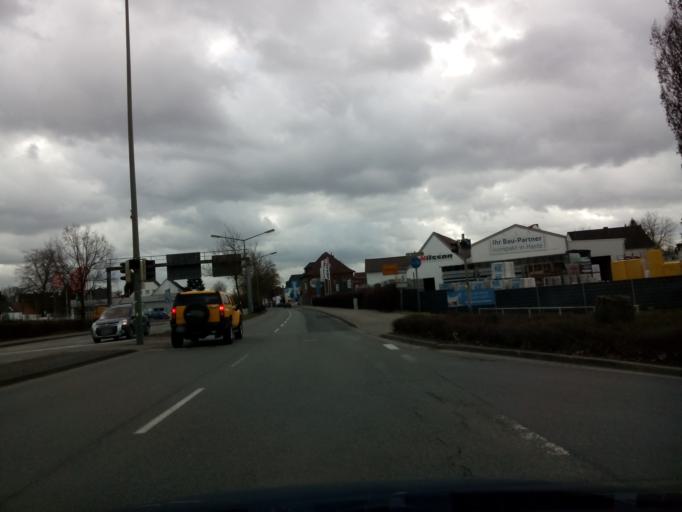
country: DE
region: Lower Saxony
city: Osnabrueck
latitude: 52.3029
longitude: 8.0344
